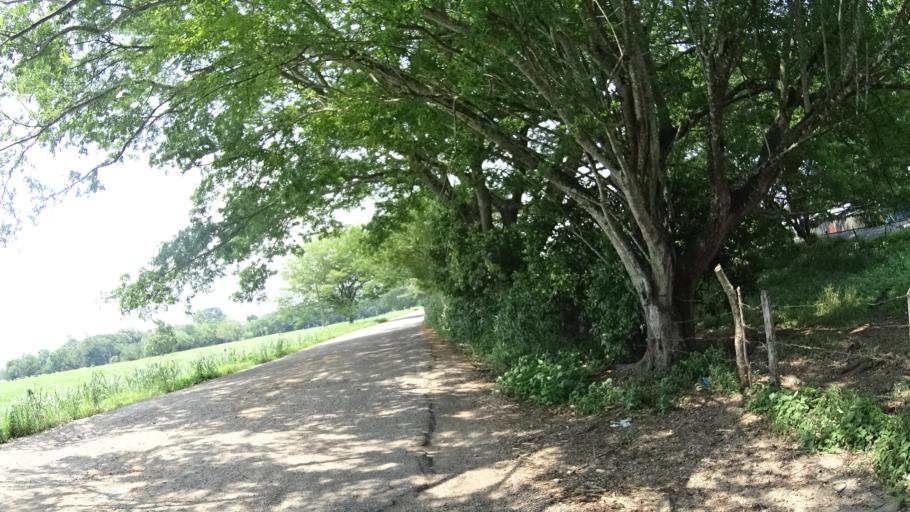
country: CO
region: Cundinamarca
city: Puerto Salgar
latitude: 5.5051
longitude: -74.6891
